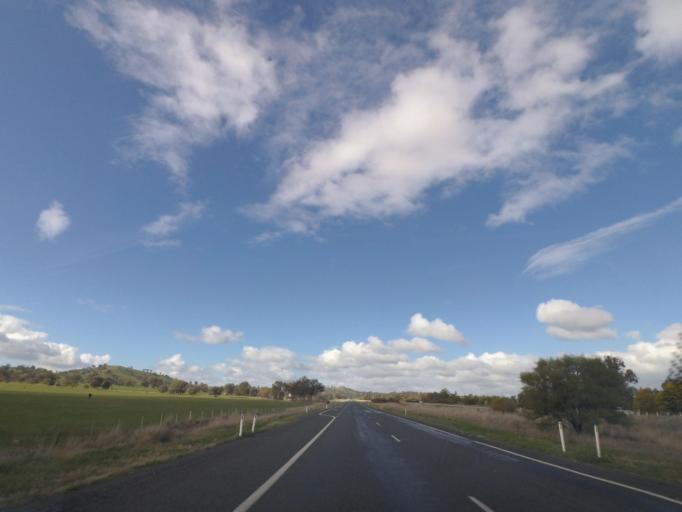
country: AU
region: New South Wales
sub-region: Greater Hume Shire
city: Jindera
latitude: -35.9250
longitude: 147.0650
